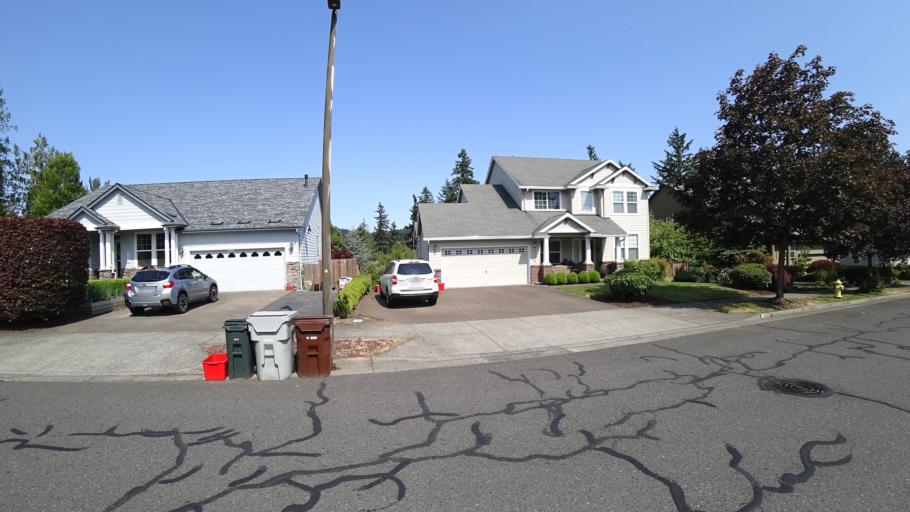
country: US
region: Oregon
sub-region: Clackamas County
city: Happy Valley
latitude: 45.4427
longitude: -122.5336
